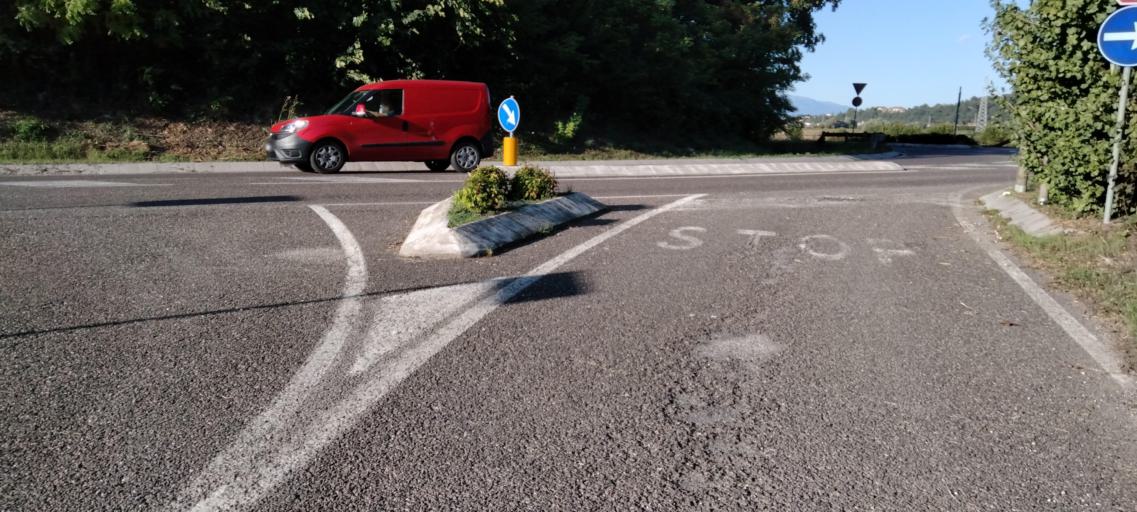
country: IT
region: Veneto
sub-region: Provincia di Vicenza
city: Creazzo
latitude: 45.5531
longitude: 11.4852
